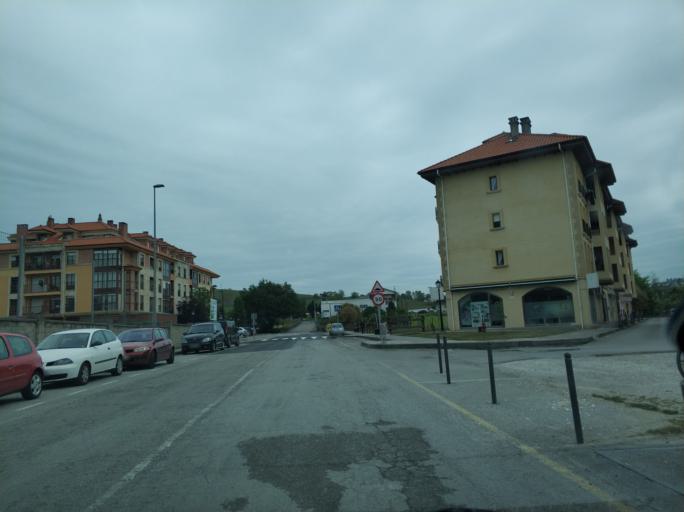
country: ES
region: Cantabria
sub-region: Provincia de Cantabria
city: Santa Maria de Cayon
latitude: 43.3216
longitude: -3.8565
